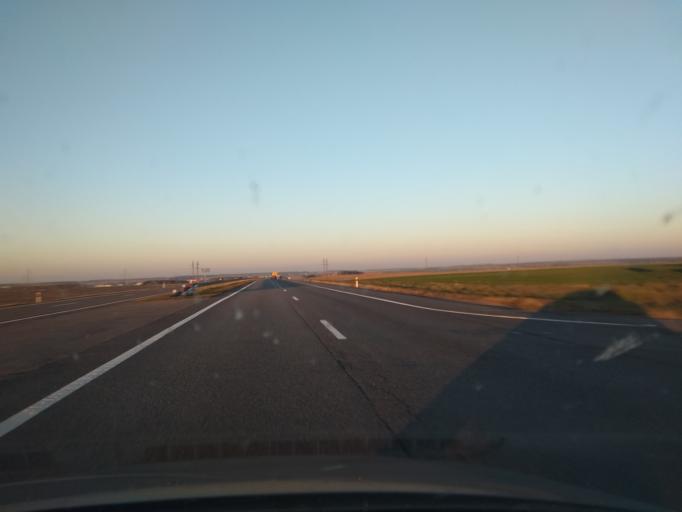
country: BY
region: Minsk
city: Snow
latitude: 53.3214
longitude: 26.4078
